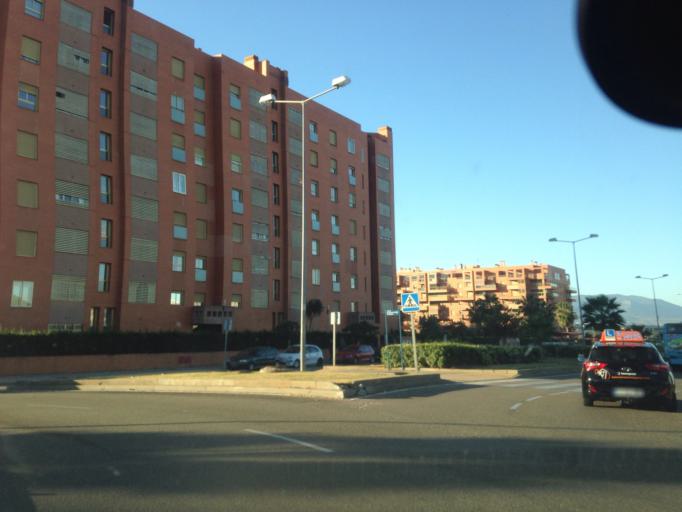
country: ES
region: Andalusia
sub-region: Provincia de Malaga
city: Malaga
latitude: 36.7200
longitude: -4.4851
